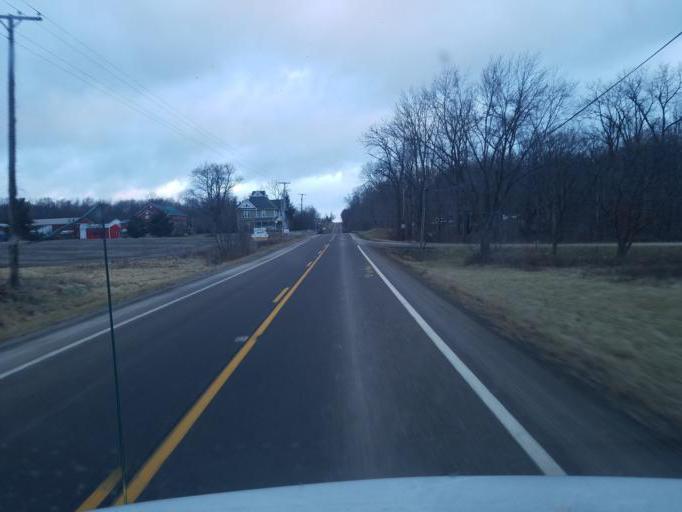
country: US
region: Ohio
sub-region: Richland County
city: Lexington
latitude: 40.5719
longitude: -82.6647
